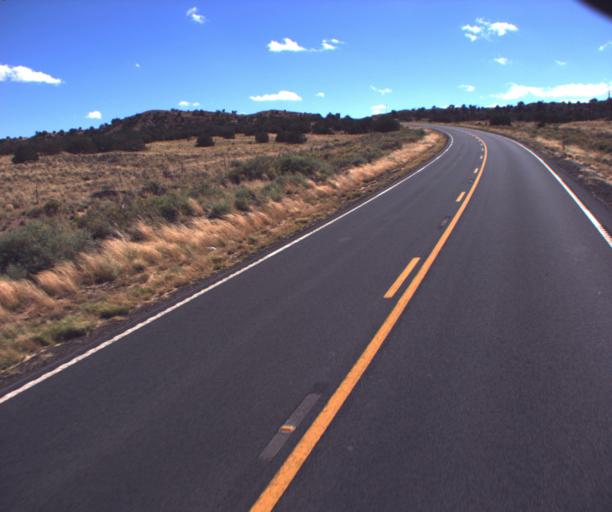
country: US
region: Arizona
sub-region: Apache County
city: Houck
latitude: 35.0375
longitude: -109.2665
